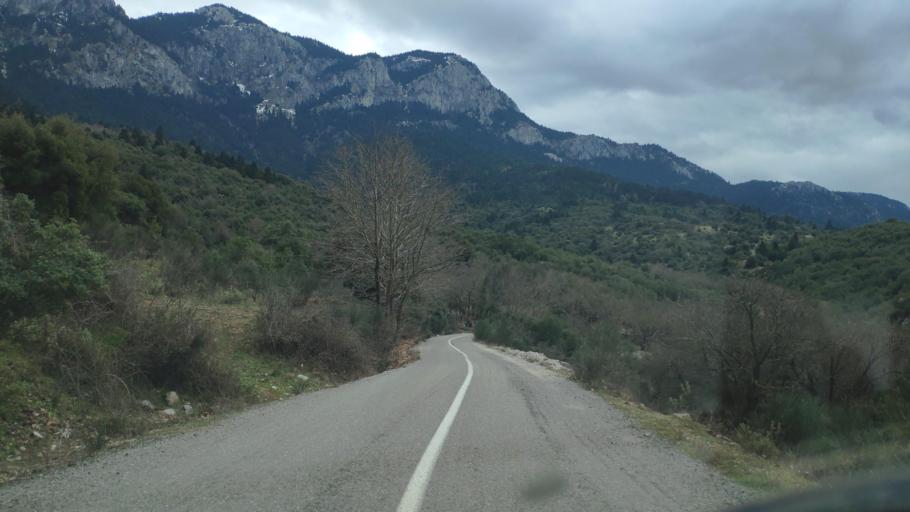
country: GR
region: Central Greece
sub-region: Nomos Fokidos
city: Amfissa
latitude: 38.6415
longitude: 22.4171
